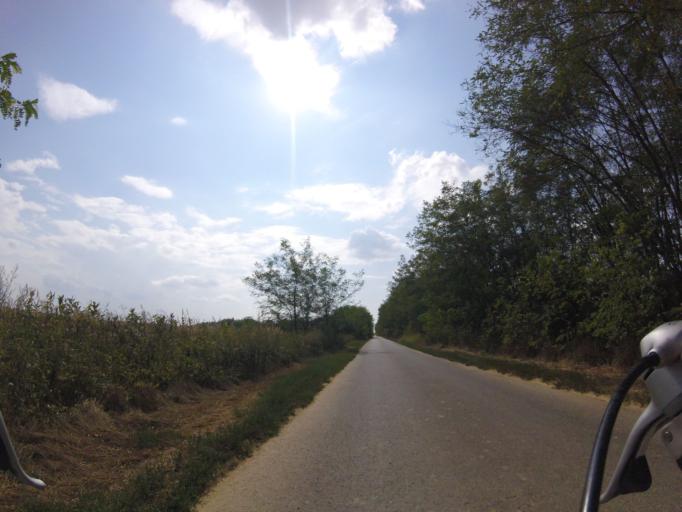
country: HU
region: Szabolcs-Szatmar-Bereg
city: Anarcs
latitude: 48.1633
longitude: 22.1770
